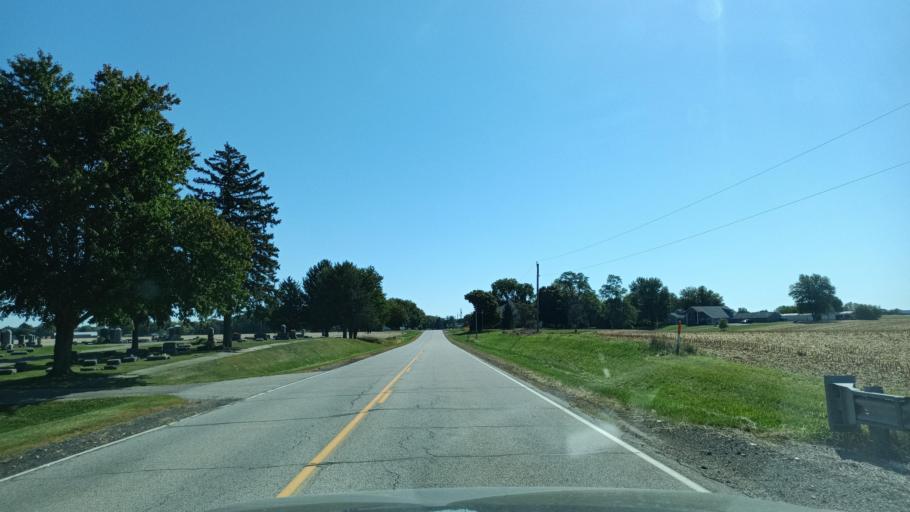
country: US
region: Illinois
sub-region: Peoria County
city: Elmwood
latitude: 40.8425
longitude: -89.8977
